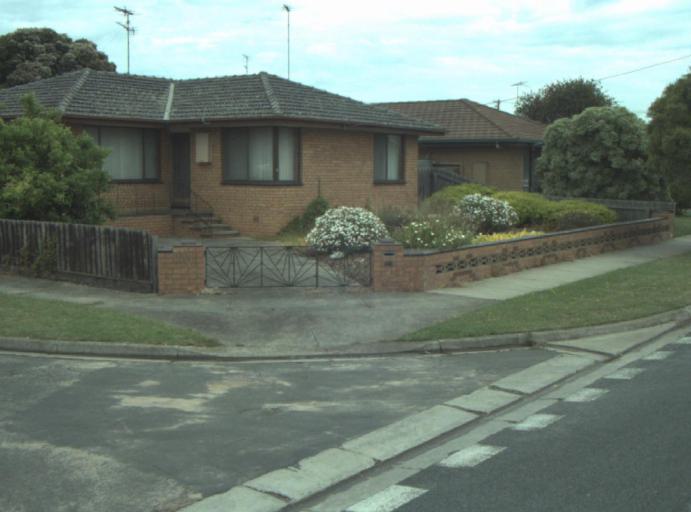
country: AU
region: Victoria
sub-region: Greater Geelong
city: Breakwater
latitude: -38.1816
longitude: 144.3924
